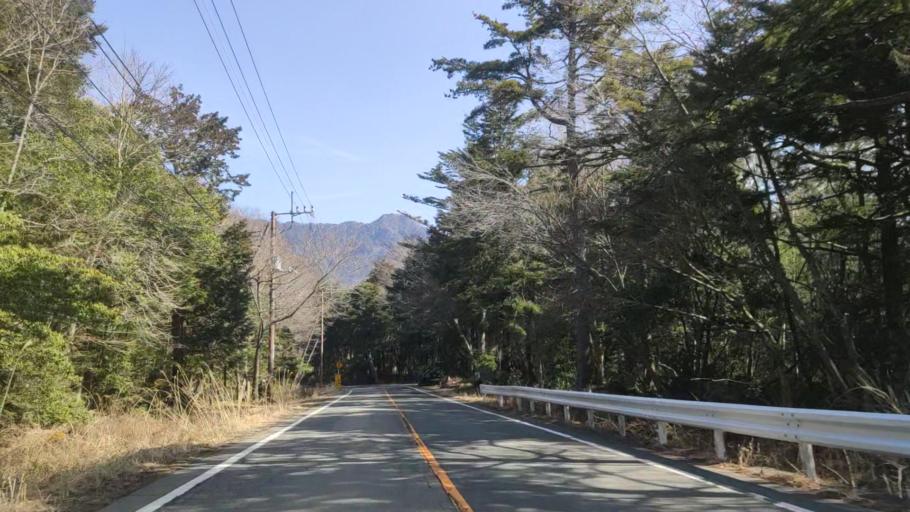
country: JP
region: Yamanashi
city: Fujikawaguchiko
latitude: 35.4897
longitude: 138.6693
